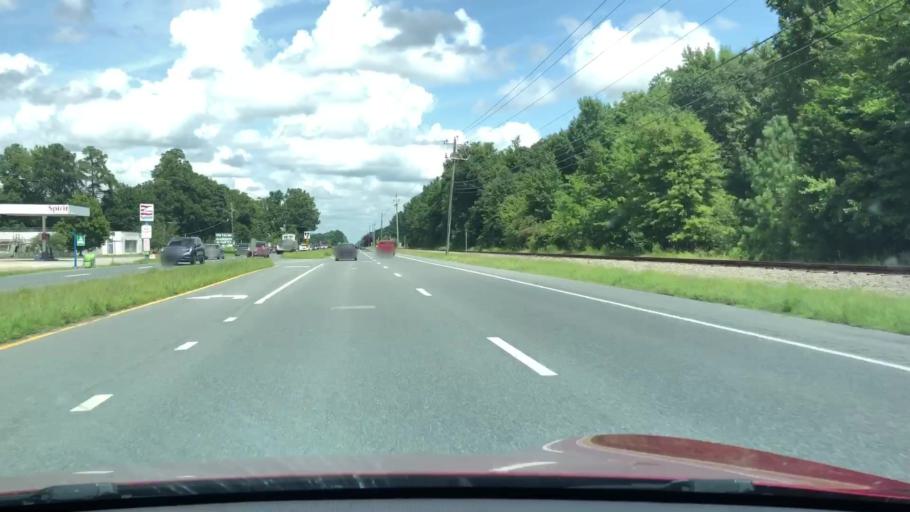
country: US
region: Virginia
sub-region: Northampton County
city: Exmore
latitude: 37.4545
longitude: -75.8720
